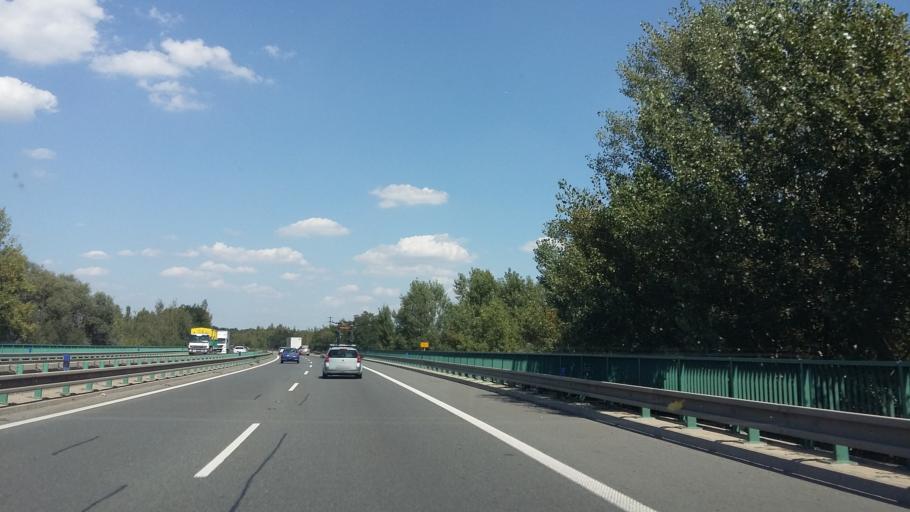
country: CZ
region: Central Bohemia
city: Brandys nad Labem-Stara Boleslav
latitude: 50.1802
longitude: 14.6921
